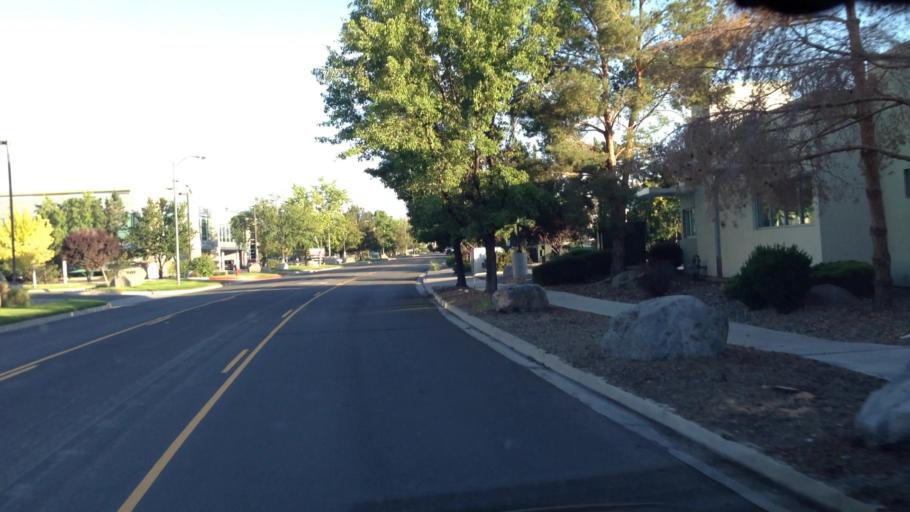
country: US
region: Nevada
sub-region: Washoe County
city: Sparks
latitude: 39.4435
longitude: -119.7627
